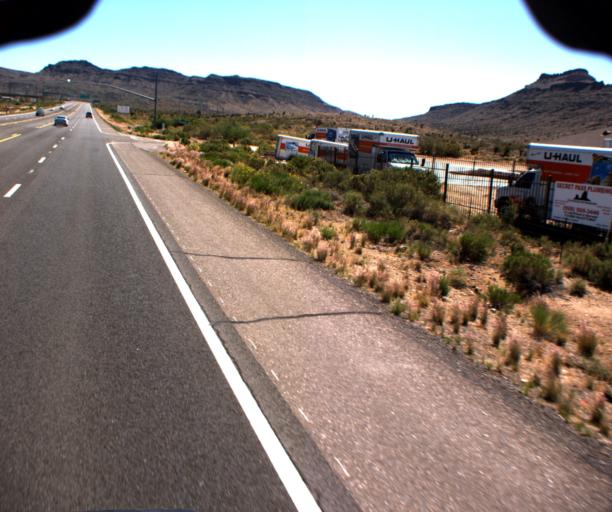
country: US
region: Arizona
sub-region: Mohave County
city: Golden Valley
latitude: 35.2186
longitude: -114.1393
